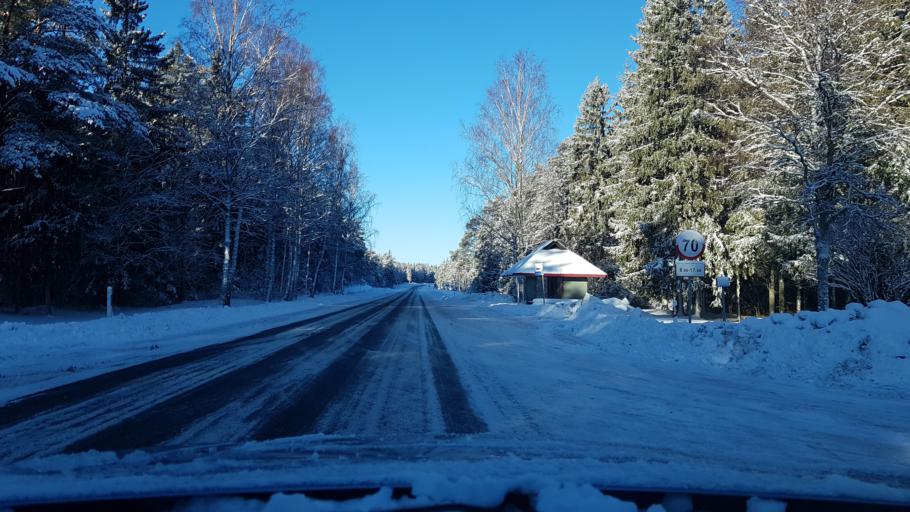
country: EE
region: Hiiumaa
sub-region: Kaerdla linn
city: Kardla
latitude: 58.9626
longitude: 22.8443
